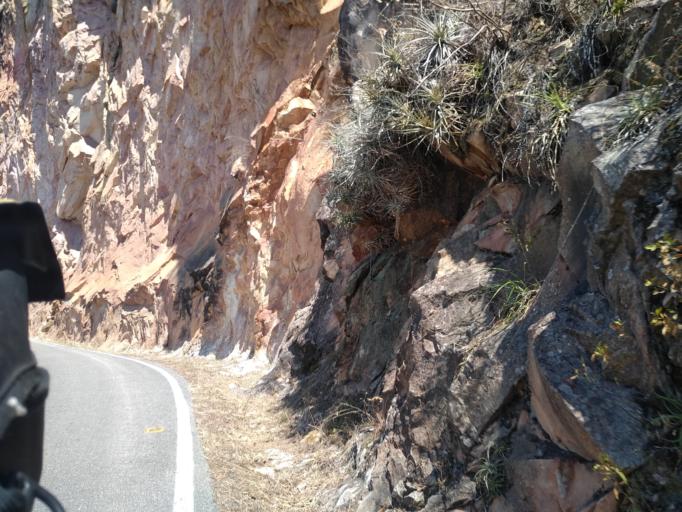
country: PE
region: Amazonas
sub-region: Provincia de Chachapoyas
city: Balsas
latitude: -6.8485
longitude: -77.9774
